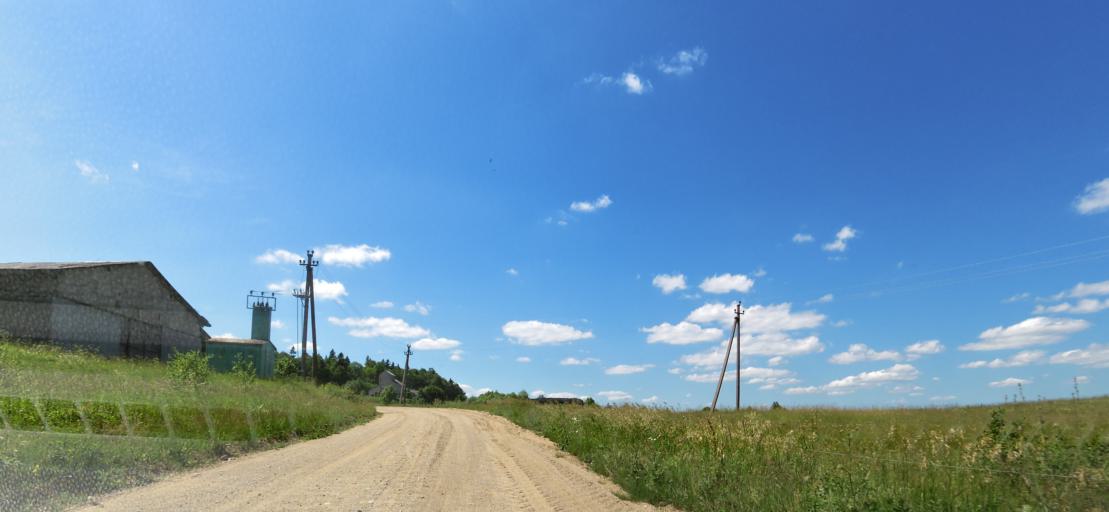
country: LT
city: Nemencine
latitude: 54.9014
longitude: 25.4850
